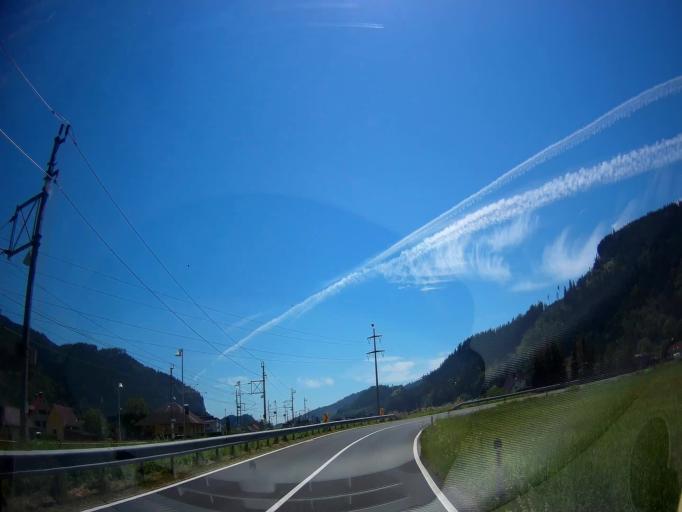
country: AT
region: Carinthia
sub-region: Politischer Bezirk Sankt Veit an der Glan
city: Micheldorf
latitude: 46.9153
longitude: 14.4311
